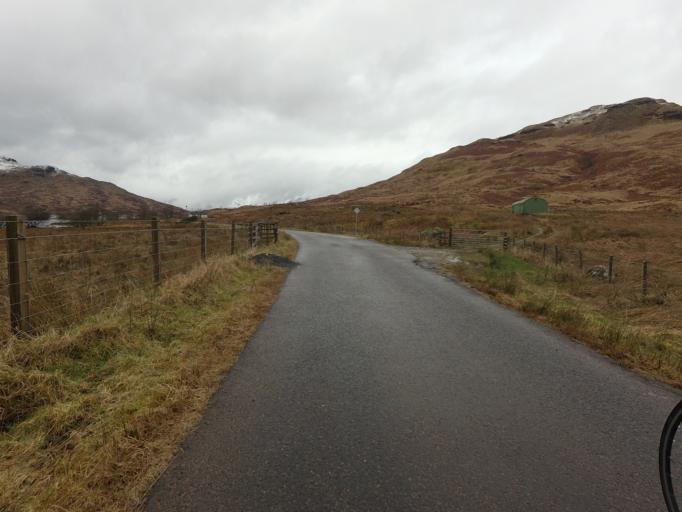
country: GB
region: Scotland
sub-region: West Dunbartonshire
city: Balloch
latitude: 56.2498
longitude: -4.6253
